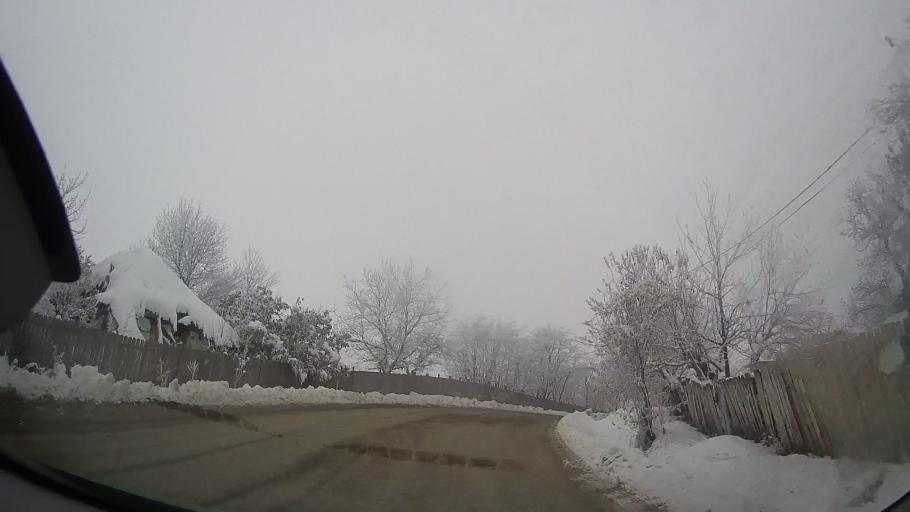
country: RO
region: Iasi
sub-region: Comuna Tansa
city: Tansa
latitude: 46.9100
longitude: 27.2257
